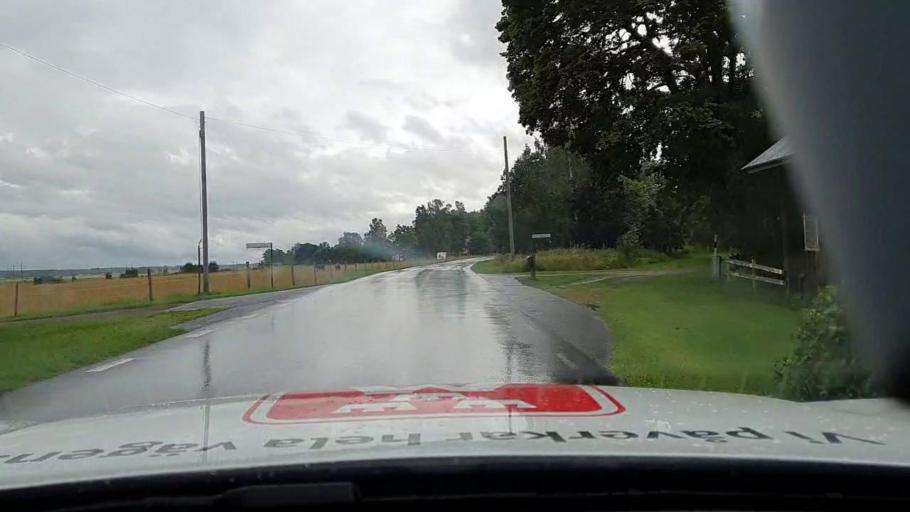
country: SE
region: Vaestra Goetaland
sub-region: Skovde Kommun
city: Stopen
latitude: 58.5518
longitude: 13.9773
